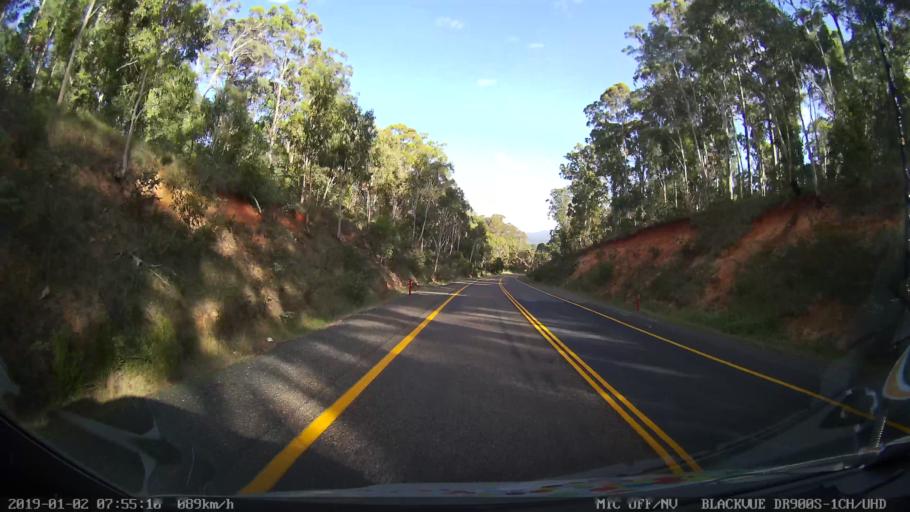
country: AU
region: New South Wales
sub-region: Tumut Shire
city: Tumut
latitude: -35.6884
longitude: 148.4888
